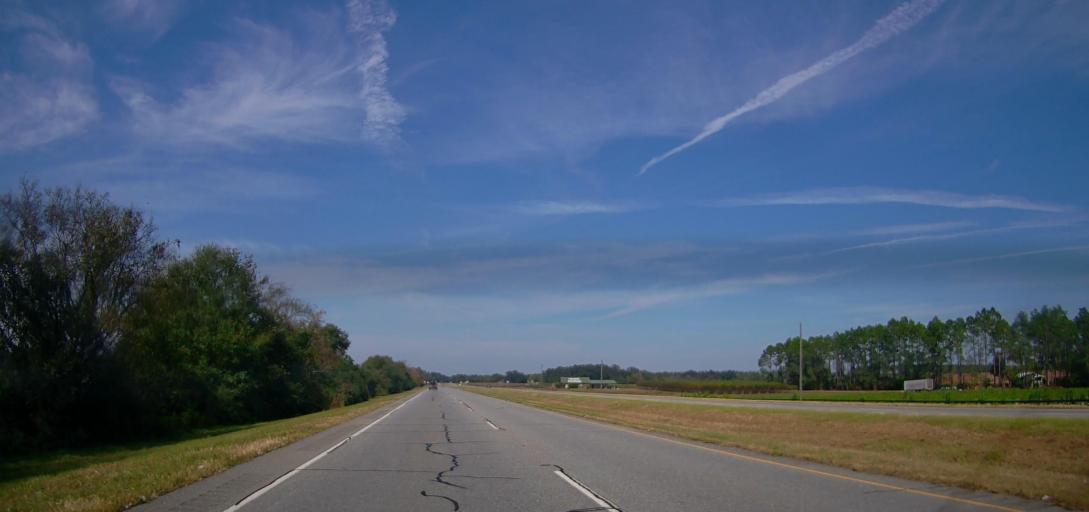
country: US
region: Georgia
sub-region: Mitchell County
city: Camilla
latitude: 31.3271
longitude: -84.1726
